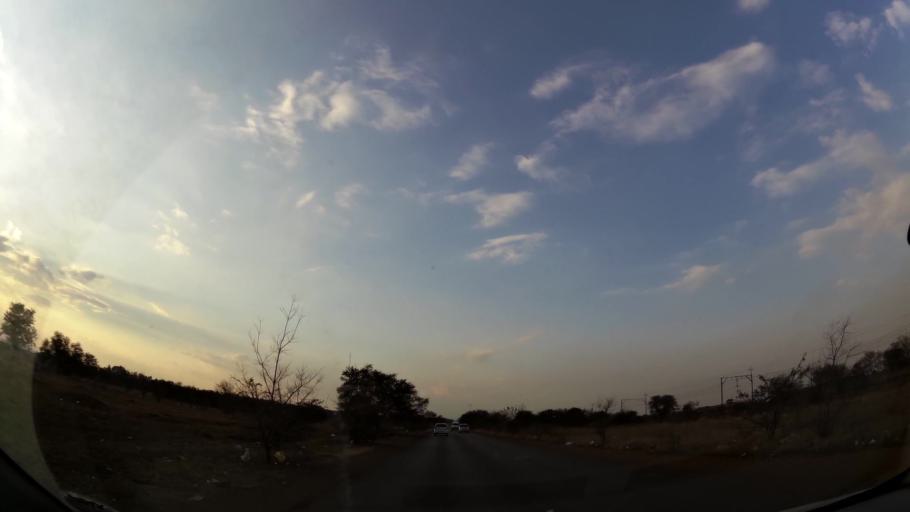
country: ZA
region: Gauteng
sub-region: City of Johannesburg Metropolitan Municipality
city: Orange Farm
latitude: -26.5724
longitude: 27.8593
